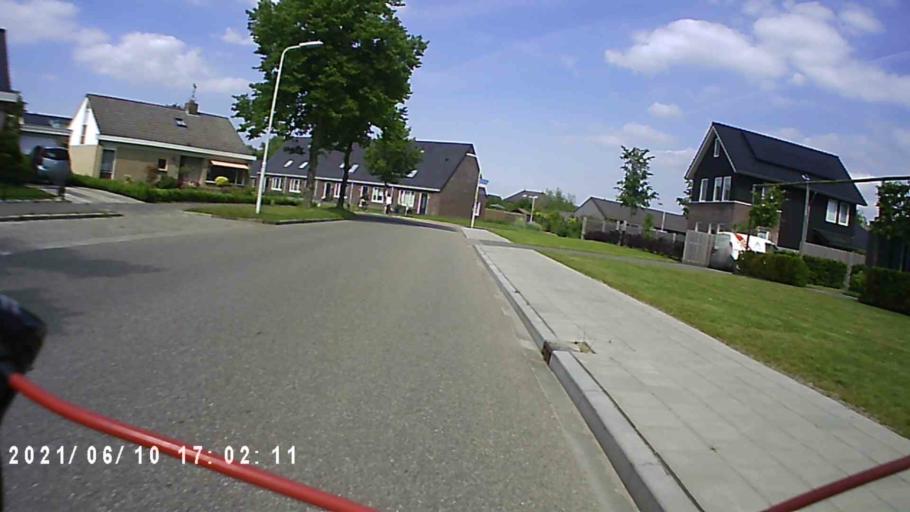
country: NL
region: Friesland
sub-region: Gemeente Kollumerland en Nieuwkruisland
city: Kollum
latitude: 53.2775
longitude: 6.1543
